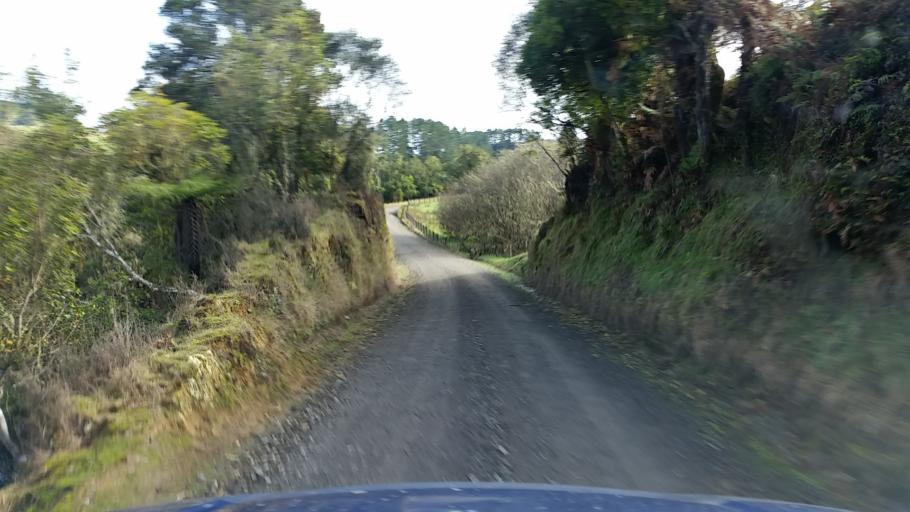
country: NZ
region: Taranaki
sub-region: New Plymouth District
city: Waitara
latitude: -39.1109
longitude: 174.8498
